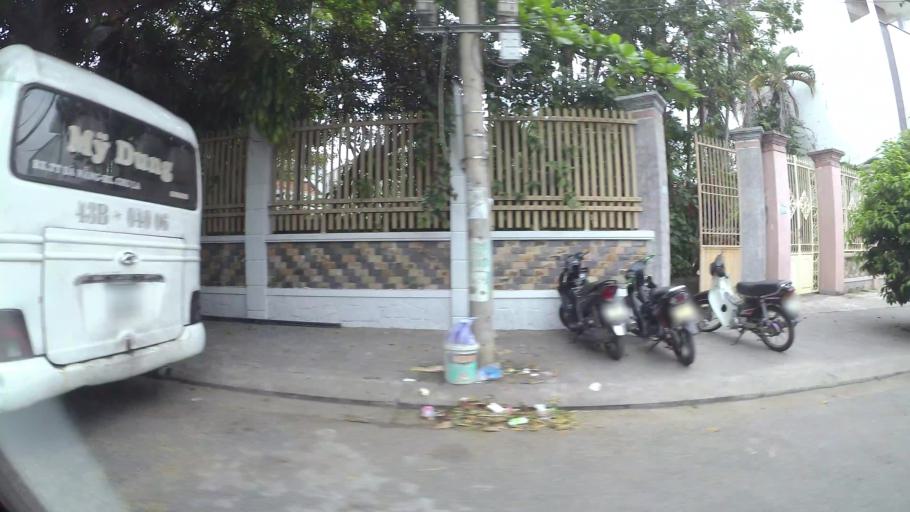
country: VN
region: Da Nang
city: Thanh Khe
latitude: 16.0611
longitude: 108.1901
